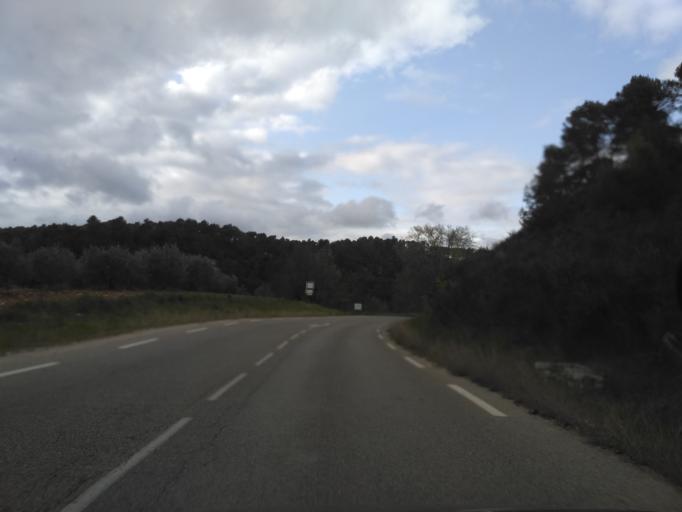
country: FR
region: Provence-Alpes-Cote d'Azur
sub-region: Departement du Var
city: Barjols
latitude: 43.5674
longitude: 6.0120
